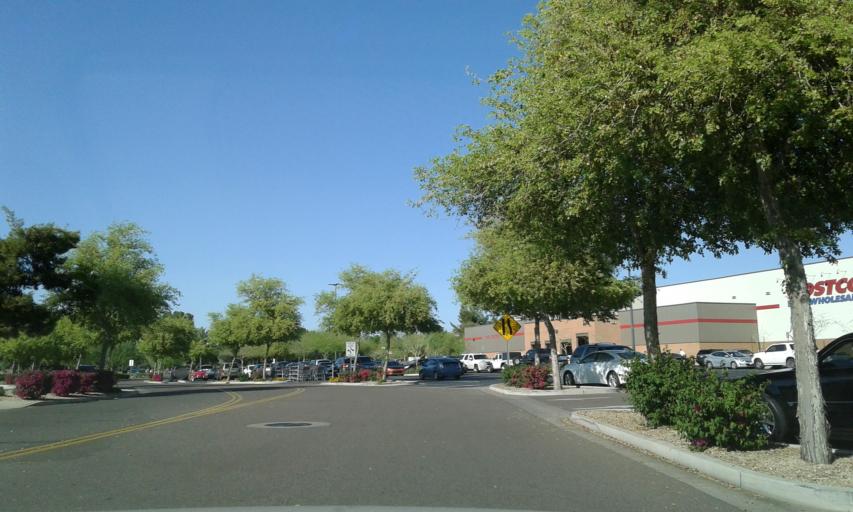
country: US
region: Arizona
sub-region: Maricopa County
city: Paradise Valley
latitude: 33.6027
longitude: -111.9874
